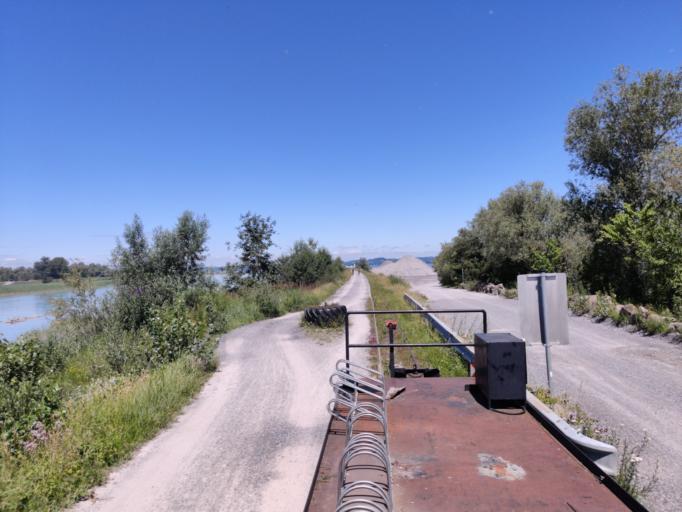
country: AT
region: Vorarlberg
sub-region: Politischer Bezirk Bregenz
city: Hard
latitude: 47.4982
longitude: 9.6720
